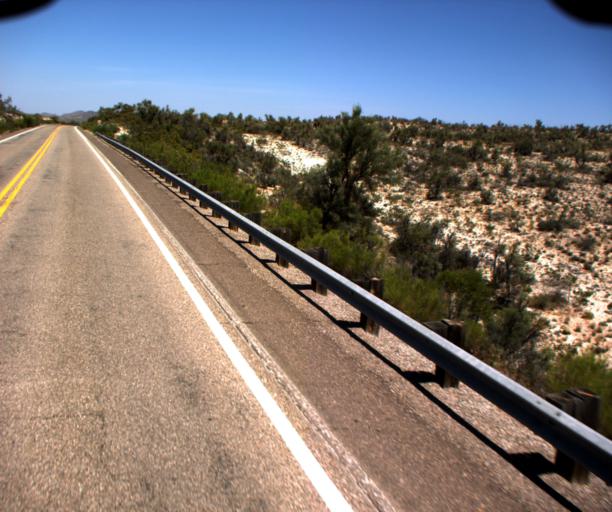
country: US
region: Arizona
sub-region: Gila County
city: Peridot
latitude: 33.2560
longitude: -110.2863
